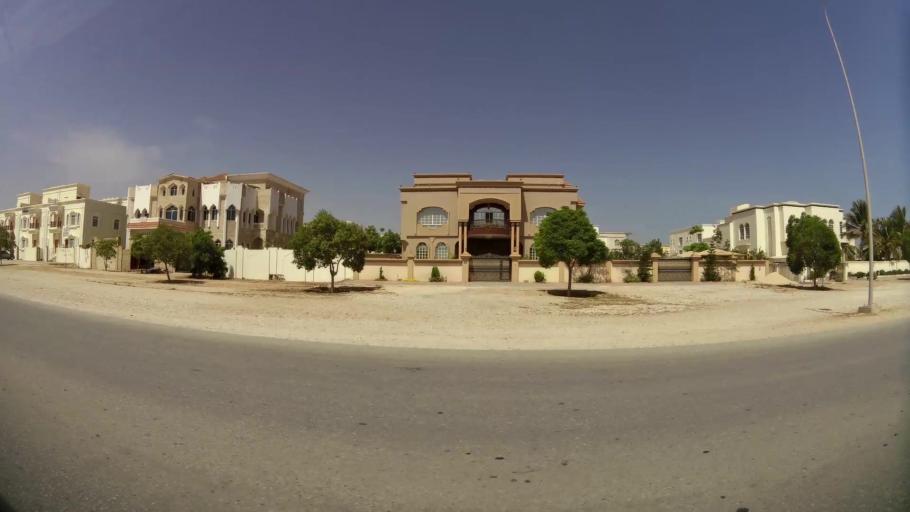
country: OM
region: Zufar
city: Salalah
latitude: 17.0465
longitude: 54.1490
